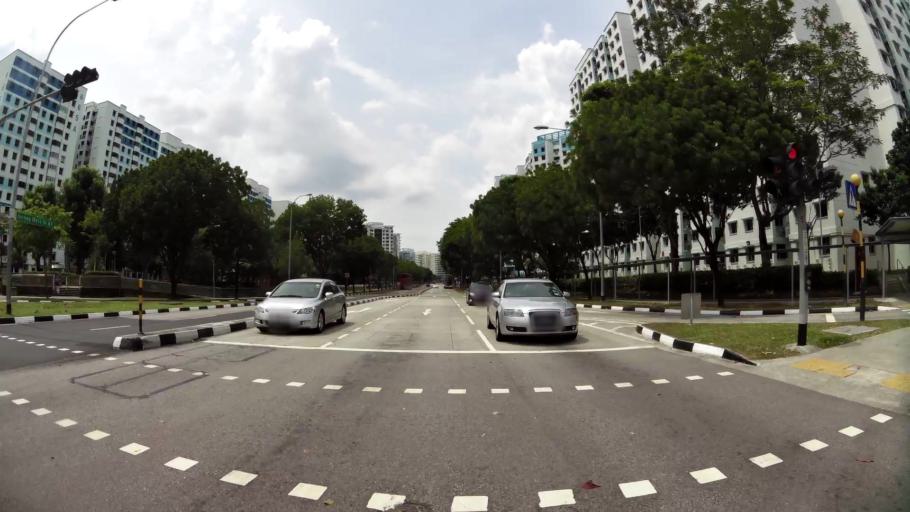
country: MY
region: Johor
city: Johor Bahru
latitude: 1.3411
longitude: 103.7038
